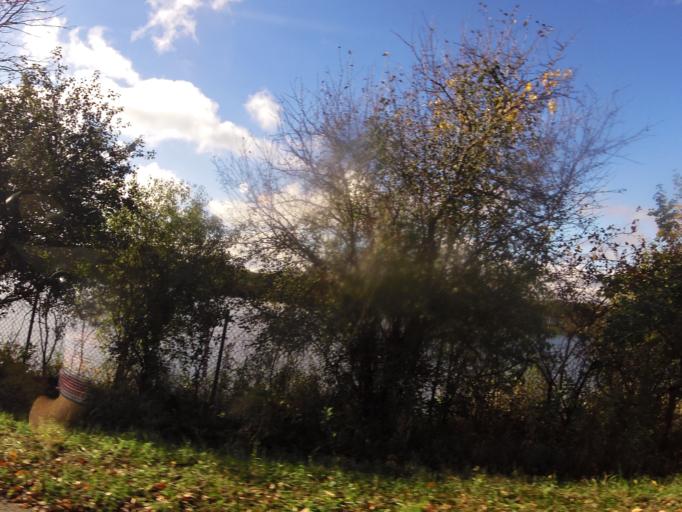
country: US
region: Minnesota
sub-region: Dakota County
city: Eagan
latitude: 44.8237
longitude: -93.2240
